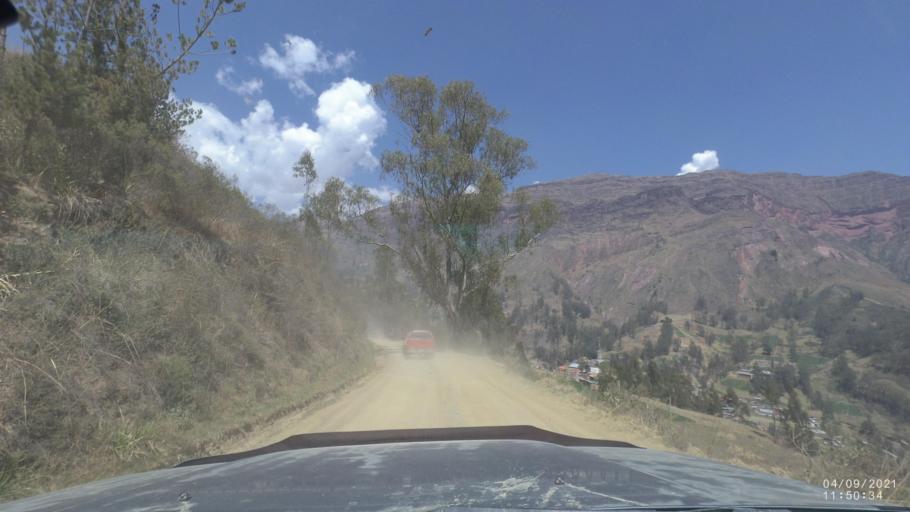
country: BO
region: Cochabamba
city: Colchani
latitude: -17.2269
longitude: -66.5258
